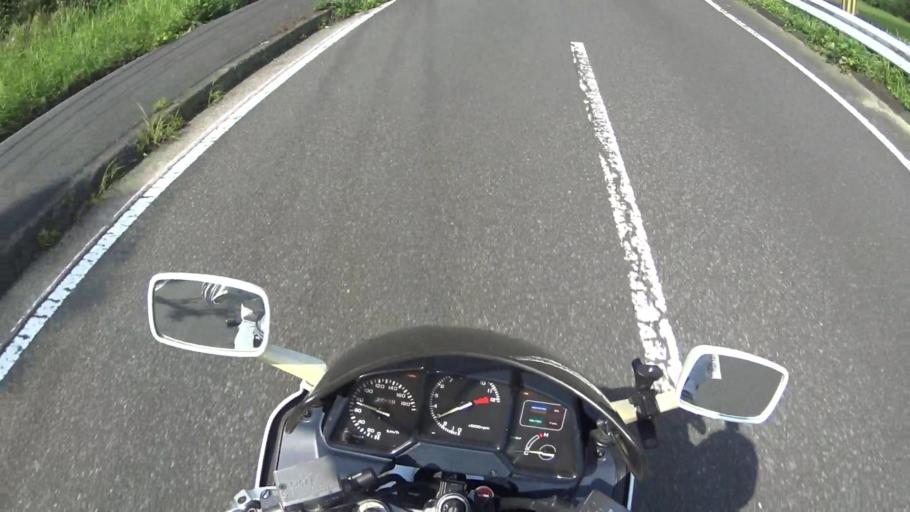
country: JP
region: Kyoto
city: Miyazu
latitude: 35.6268
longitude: 135.2388
